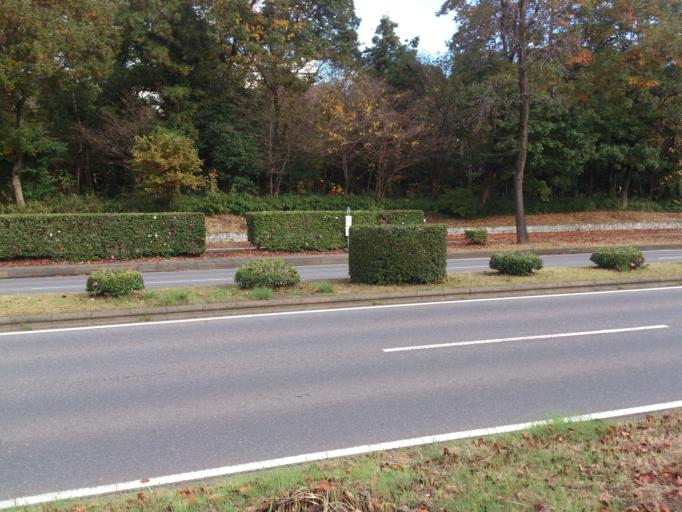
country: JP
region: Ibaraki
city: Naka
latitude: 36.0936
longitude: 140.0985
